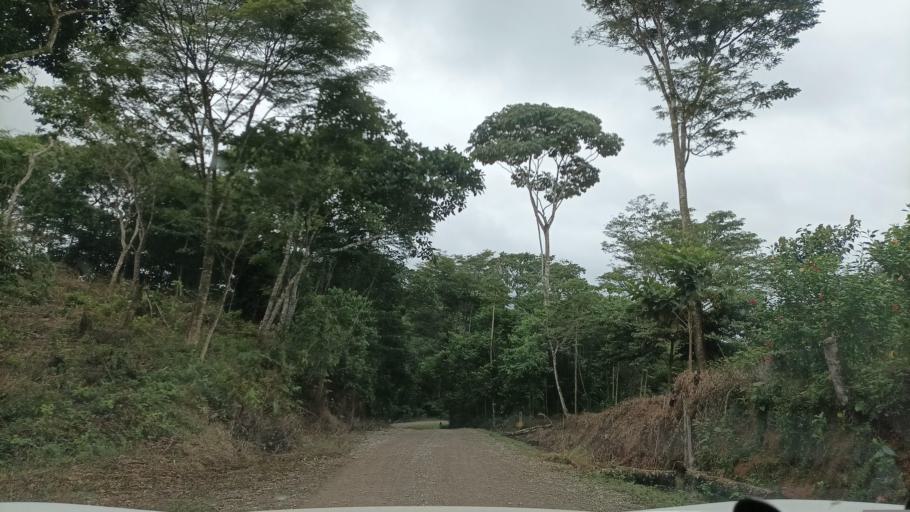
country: MX
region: Veracruz
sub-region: Uxpanapa
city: Poblado 10
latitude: 17.4309
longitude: -94.4188
